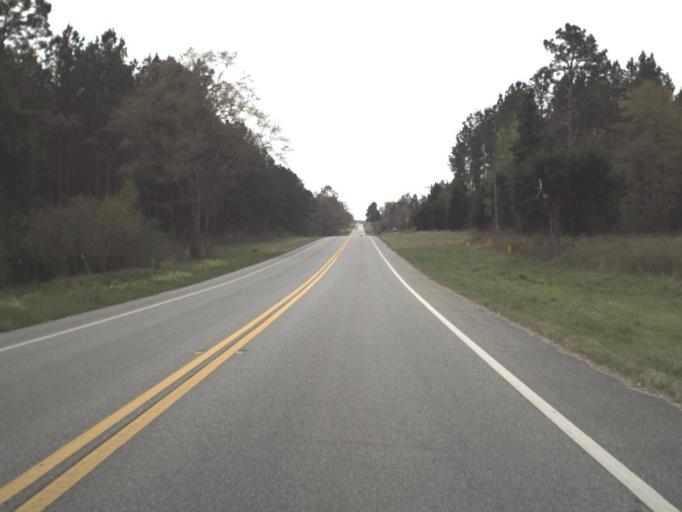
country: US
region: Florida
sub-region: Jackson County
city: Graceville
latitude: 30.9376
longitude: -85.6491
